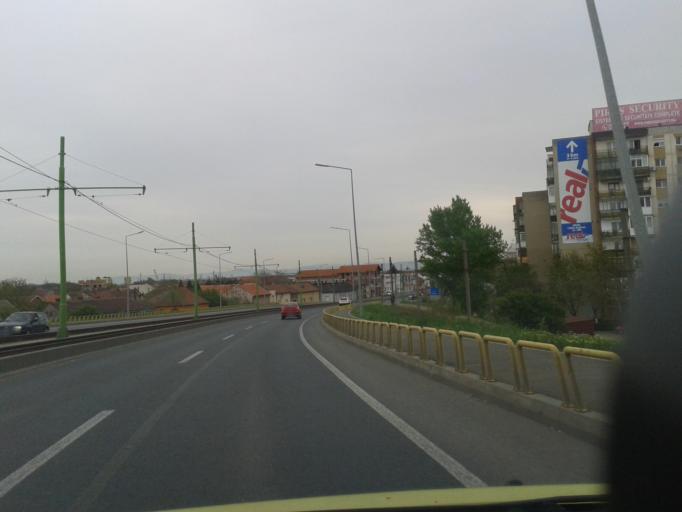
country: RO
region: Arad
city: Arad
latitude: 46.1805
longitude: 21.3393
